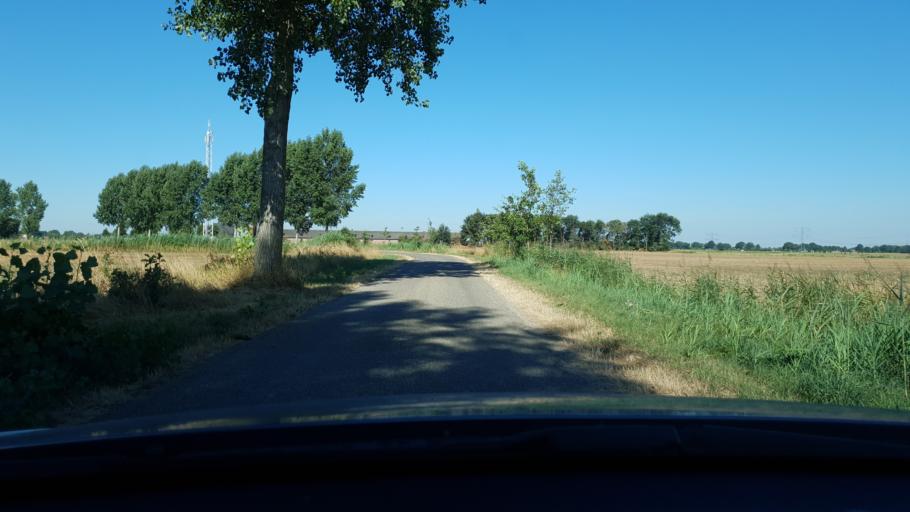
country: NL
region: North Brabant
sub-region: Gemeente Grave
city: Grave
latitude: 51.7764
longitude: 5.7583
